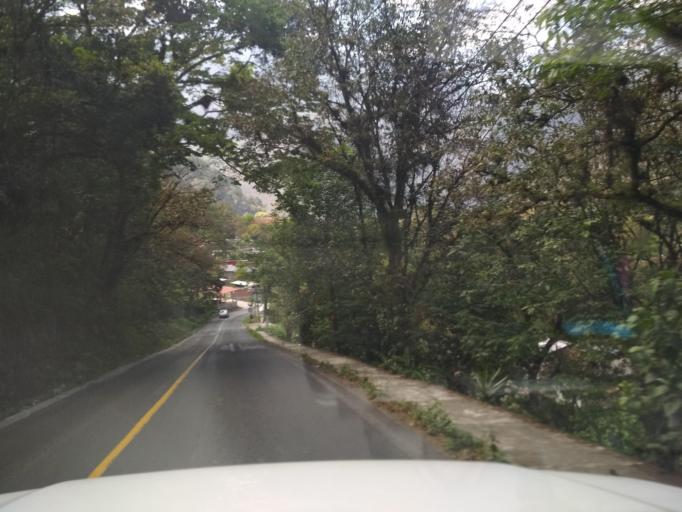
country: MX
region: Veracruz
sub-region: Tlilapan
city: Tonalixco
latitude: 18.7880
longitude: -97.0938
